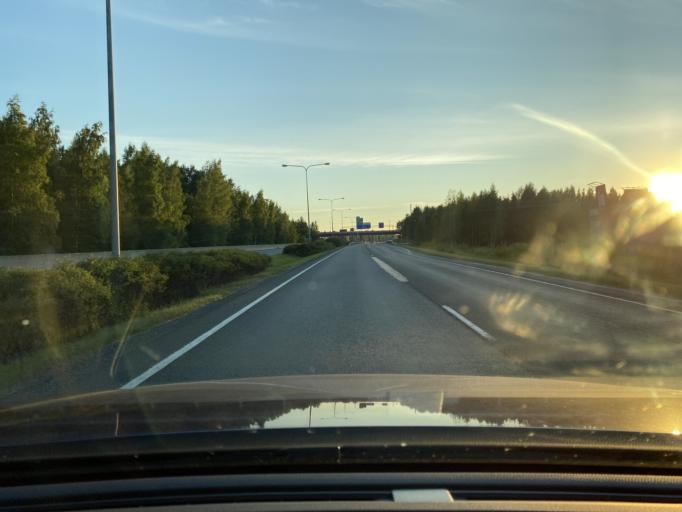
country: FI
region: Pirkanmaa
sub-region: Tampere
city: Yloejaervi
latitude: 61.5540
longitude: 23.5810
